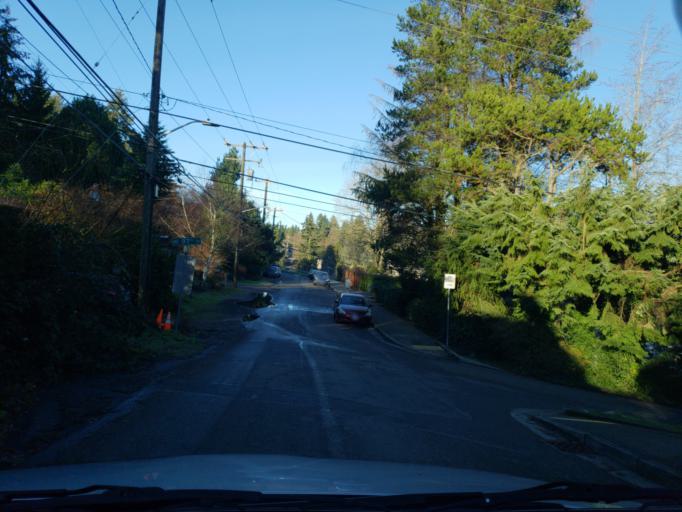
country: US
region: Washington
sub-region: King County
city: Lake Forest Park
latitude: 47.6993
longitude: -122.3069
